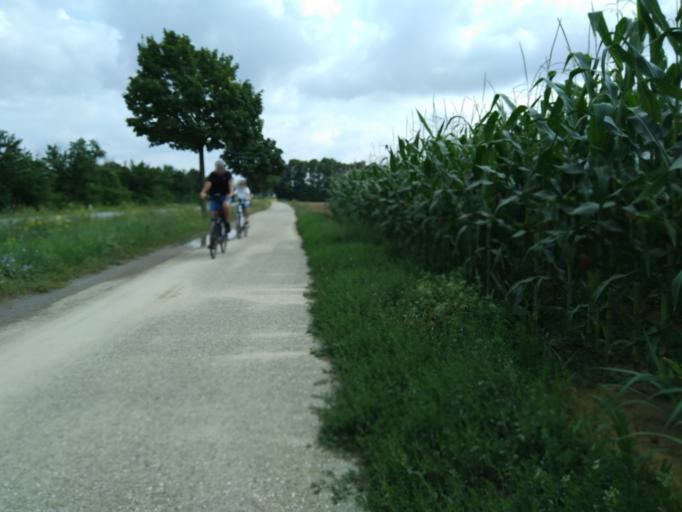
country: AT
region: Lower Austria
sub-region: Politischer Bezirk Ganserndorf
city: Gross-Schweinbarth
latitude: 48.4064
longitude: 16.6392
